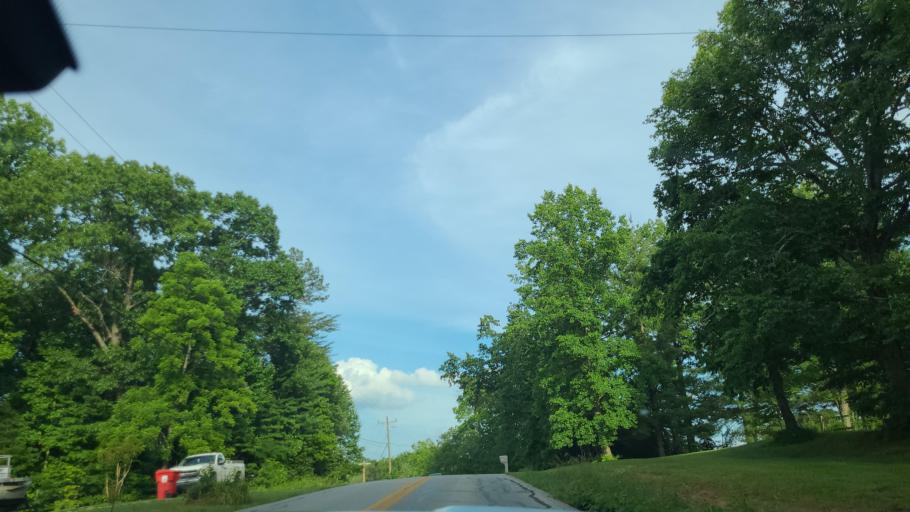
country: US
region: Kentucky
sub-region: Whitley County
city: Corbin
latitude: 36.9122
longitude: -84.2513
